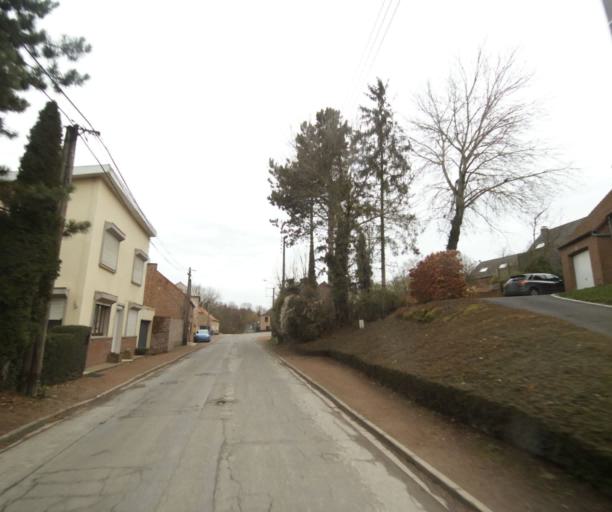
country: FR
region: Nord-Pas-de-Calais
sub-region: Departement du Nord
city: Sebourg
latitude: 50.3517
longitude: 3.6508
